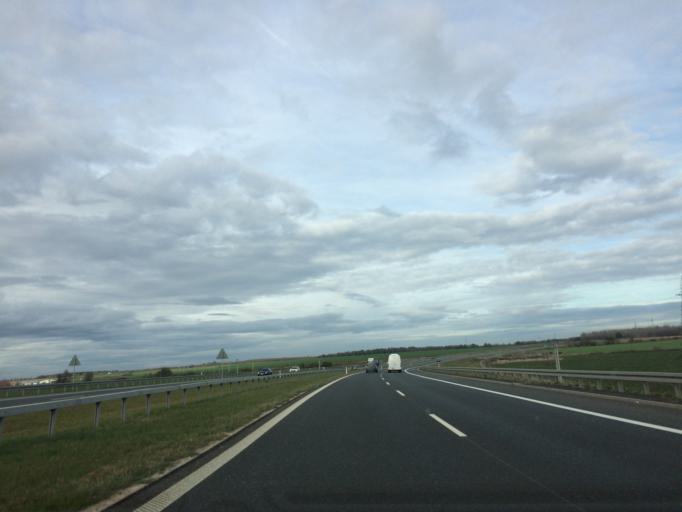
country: PL
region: Lower Silesian Voivodeship
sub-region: Powiat legnicki
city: Milkowice
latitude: 51.1843
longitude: 16.0869
